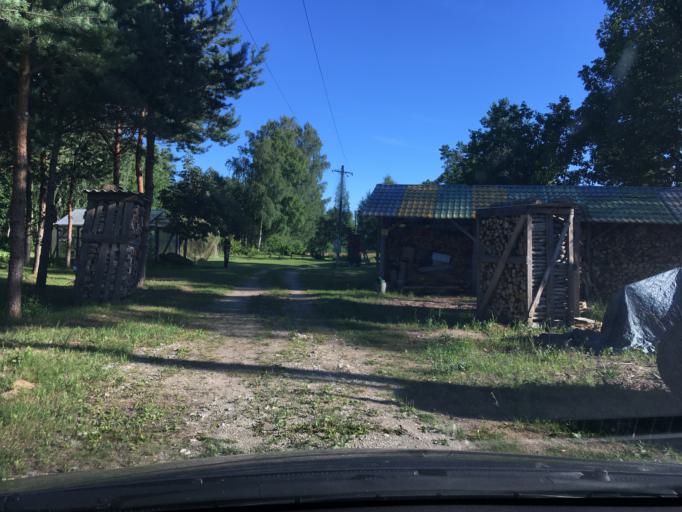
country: EE
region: Laeaene
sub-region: Lihula vald
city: Lihula
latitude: 58.5860
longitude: 23.7361
